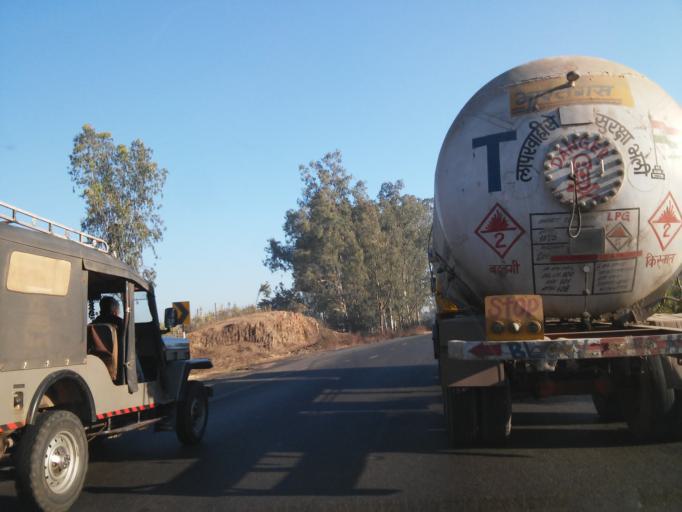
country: IN
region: Rajasthan
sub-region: Dungarpur
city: Dungarpur
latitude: 23.8650
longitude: 73.5267
